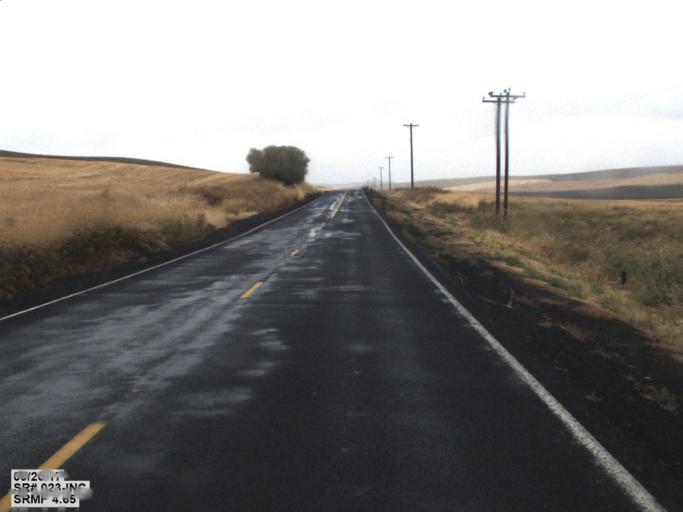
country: US
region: Washington
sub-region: Whitman County
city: Colfax
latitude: 47.0045
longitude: -117.4487
